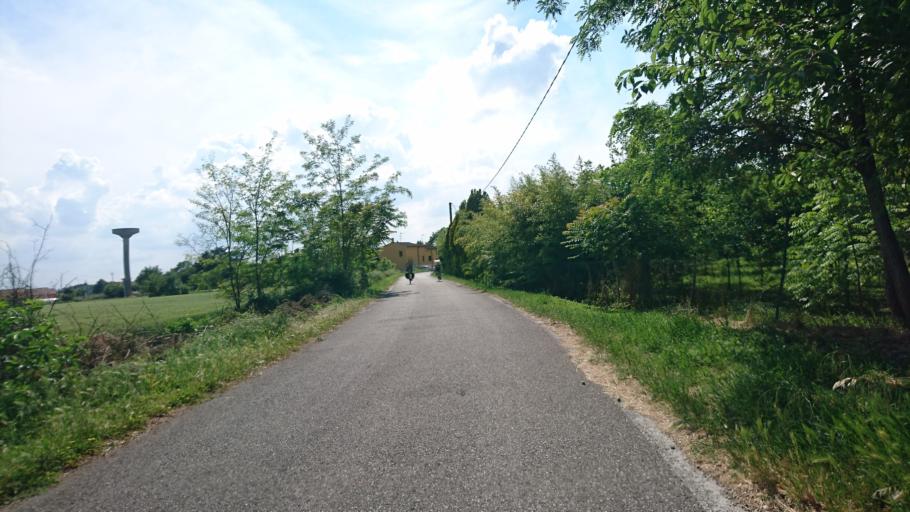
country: IT
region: Veneto
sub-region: Provincia di Rovigo
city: Castelnovo Bariano
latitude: 45.0272
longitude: 11.2992
